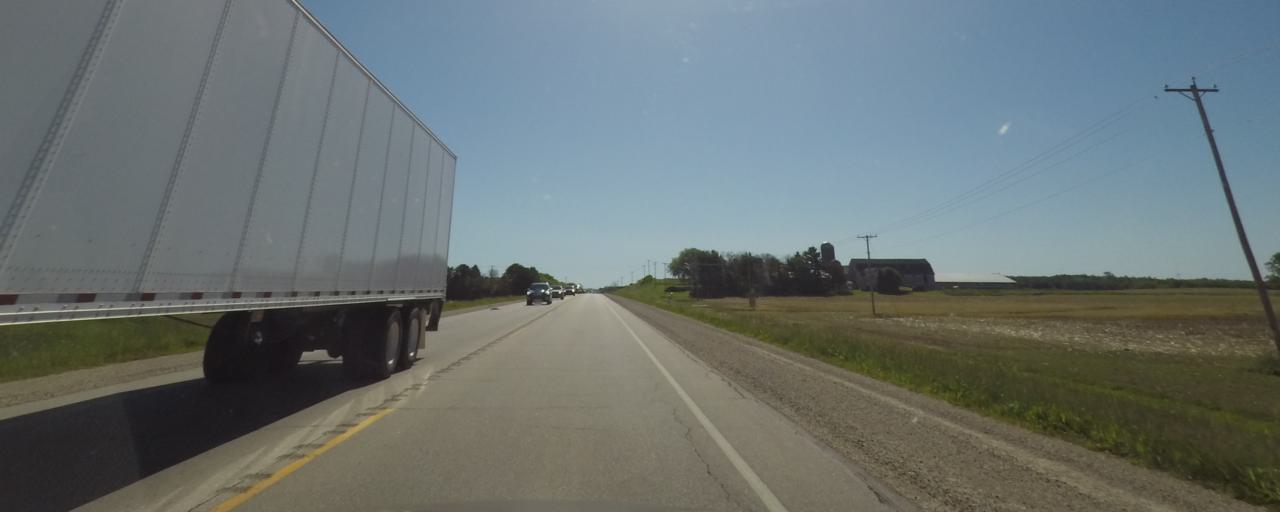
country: US
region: Wisconsin
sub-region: Fond du Lac County
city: Saint Peter
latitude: 43.7835
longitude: -88.3453
